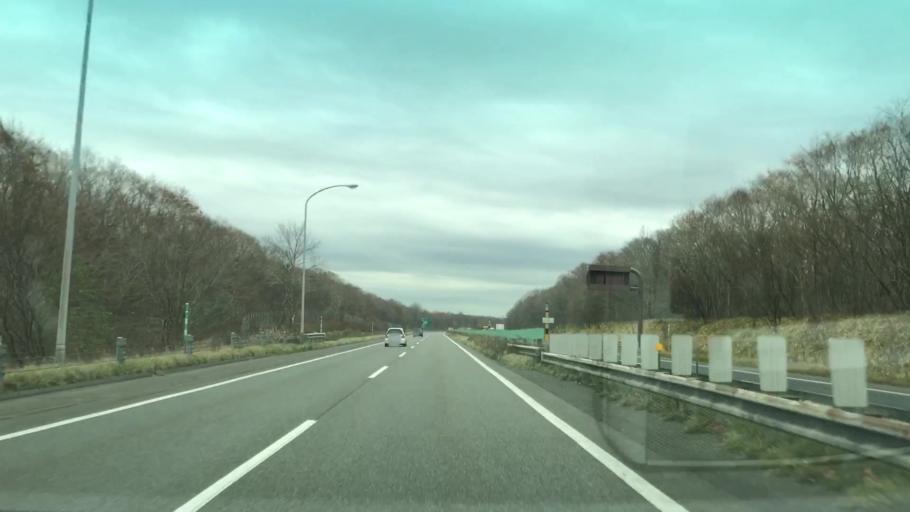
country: JP
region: Hokkaido
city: Chitose
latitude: 42.8036
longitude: 141.6245
